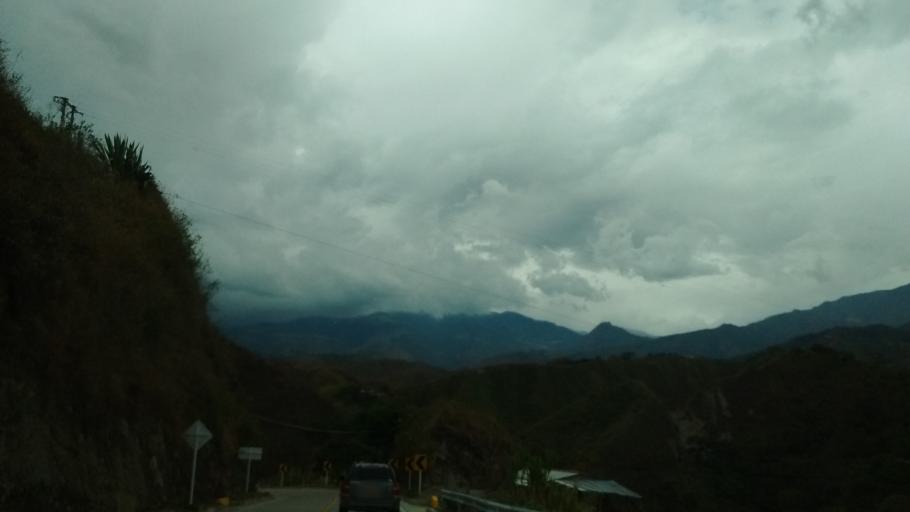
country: CO
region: Cauca
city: La Sierra
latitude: 2.1598
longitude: -76.7698
